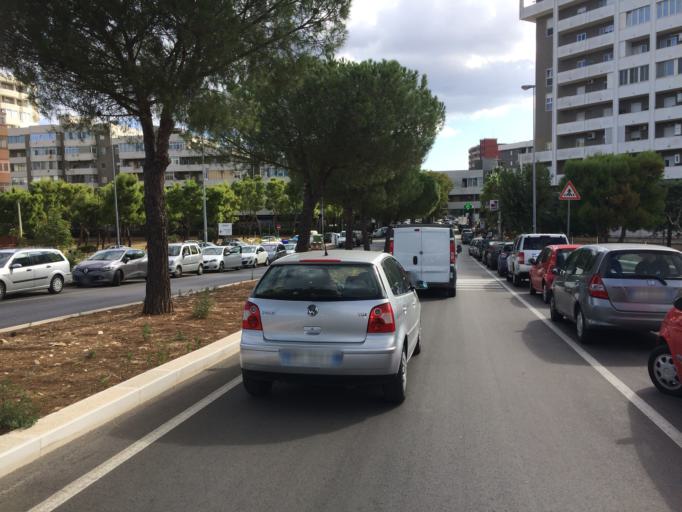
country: IT
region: Apulia
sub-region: Provincia di Bari
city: Bari
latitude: 41.0932
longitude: 16.8585
